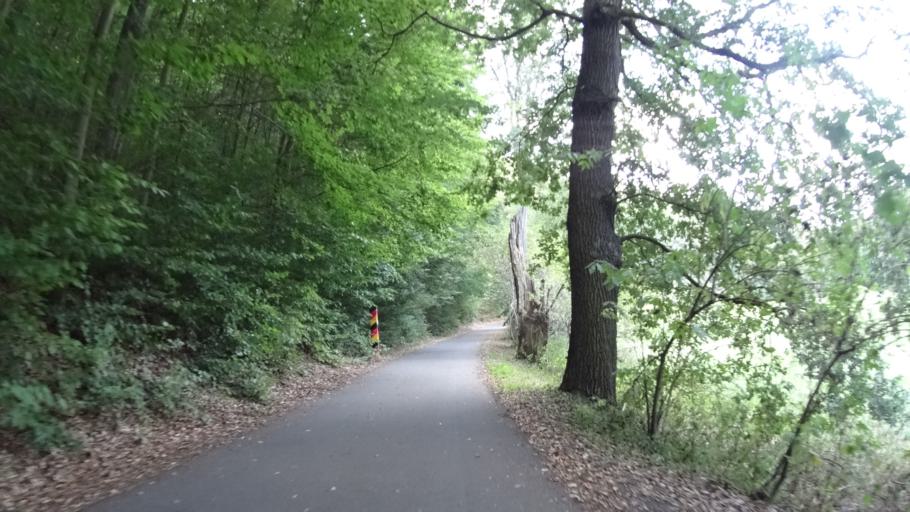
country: DE
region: Saxony
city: Ostritz
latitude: 50.9966
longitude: 14.9176
